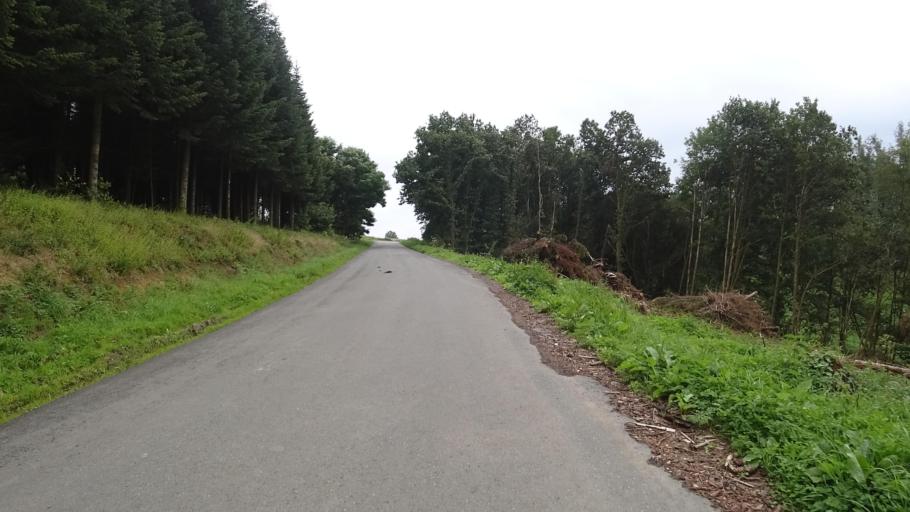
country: BE
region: Wallonia
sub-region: Province du Luxembourg
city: Chiny
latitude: 49.8010
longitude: 5.3734
